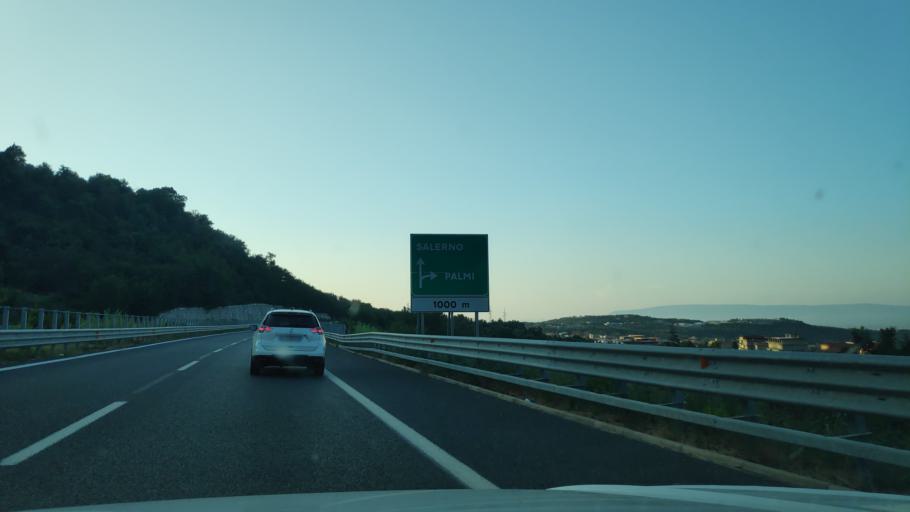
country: IT
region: Calabria
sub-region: Provincia di Reggio Calabria
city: Seminara
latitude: 38.3561
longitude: 15.8667
